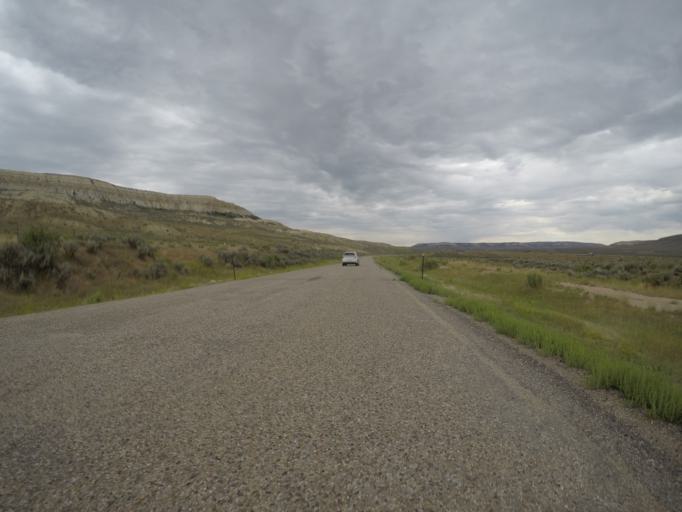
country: US
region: Wyoming
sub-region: Lincoln County
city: Kemmerer
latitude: 41.8230
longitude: -110.7390
